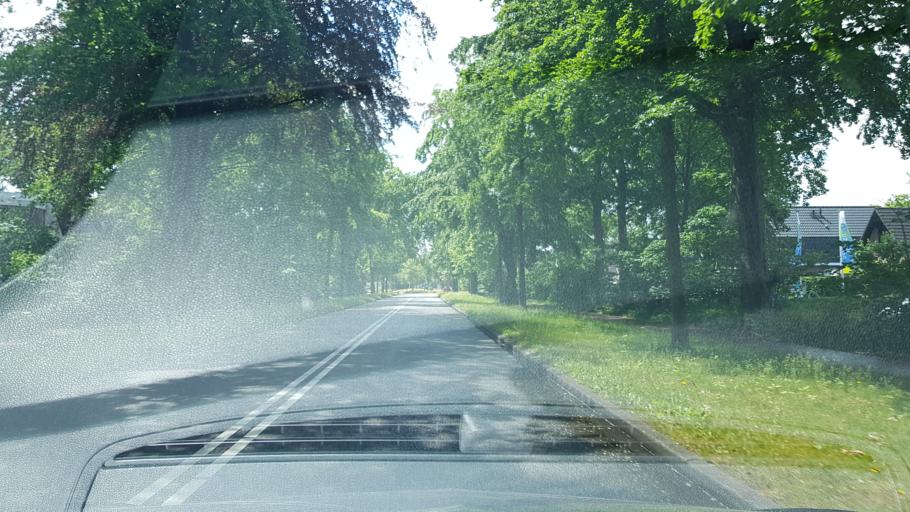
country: NL
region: Gelderland
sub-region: Gemeente Nunspeet
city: Nunspeet
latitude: 52.3794
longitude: 5.7787
